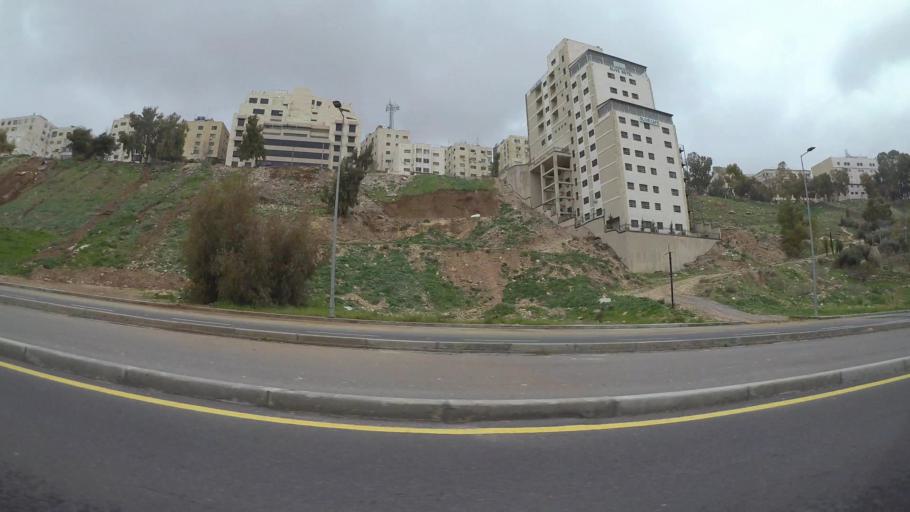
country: JO
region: Amman
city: Amman
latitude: 31.9505
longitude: 35.9012
